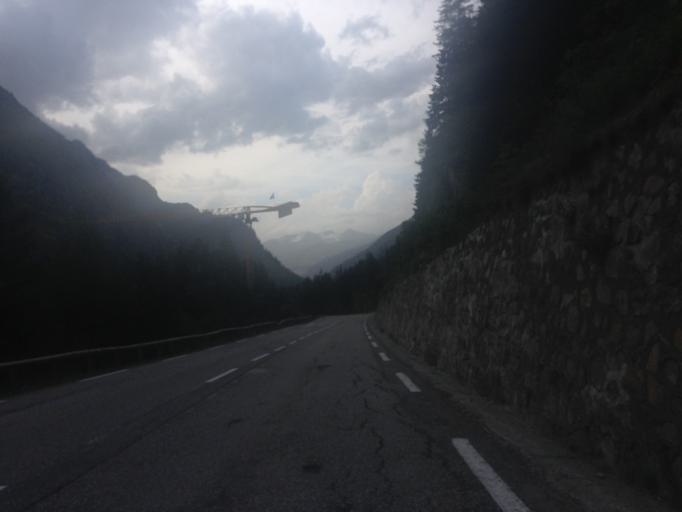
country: FR
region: Rhone-Alpes
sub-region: Departement de la Savoie
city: Tignes
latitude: 45.5151
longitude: 6.9167
